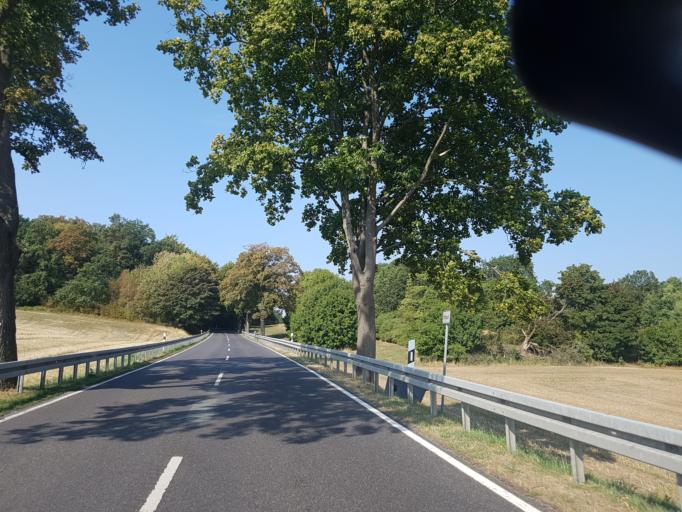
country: DE
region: Brandenburg
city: Belzig
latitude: 52.1324
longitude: 12.5276
